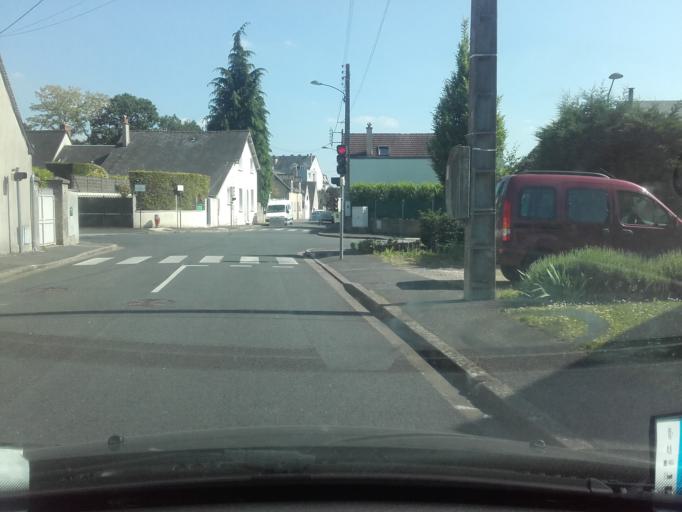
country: FR
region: Centre
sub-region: Departement d'Indre-et-Loire
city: Saint-Cyr-sur-Loire
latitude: 47.4079
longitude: 0.6715
